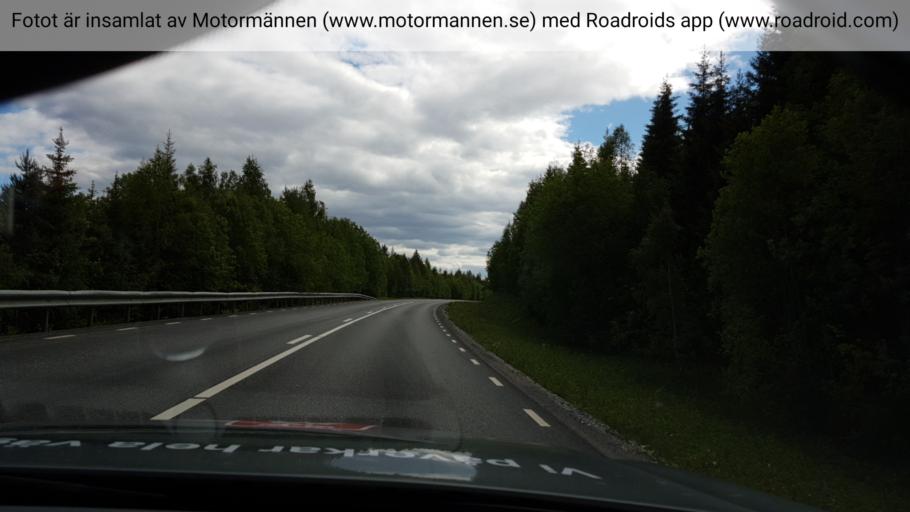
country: SE
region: Jaemtland
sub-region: Stroemsunds Kommun
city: Stroemsund
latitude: 64.0860
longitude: 15.5680
